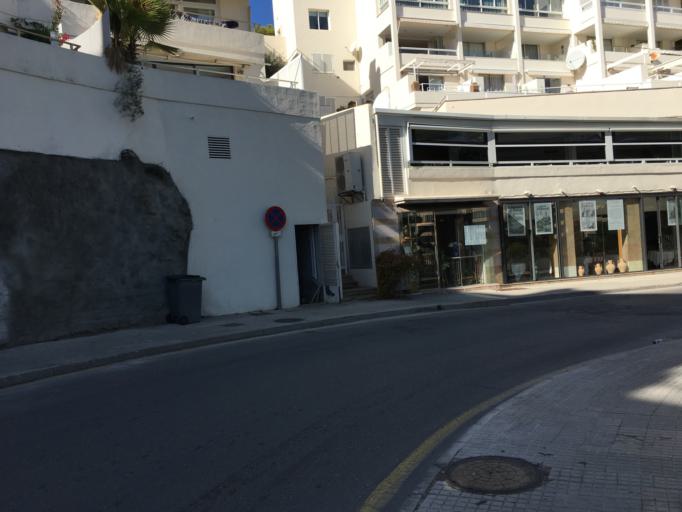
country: ES
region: Balearic Islands
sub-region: Illes Balears
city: Magaluf
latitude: 39.5363
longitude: 2.5898
